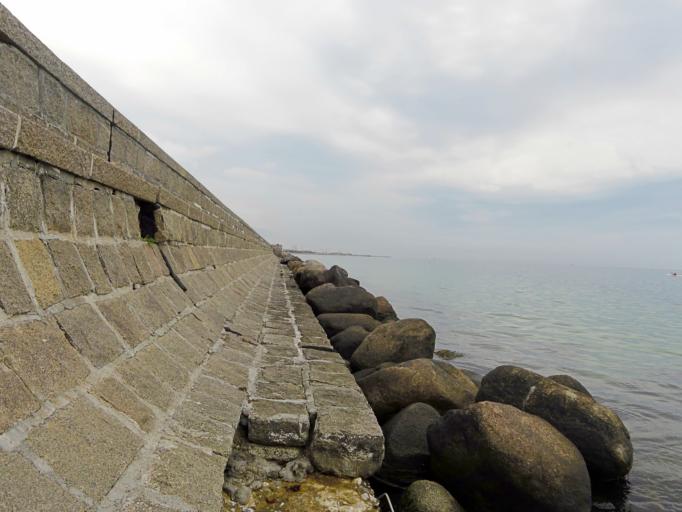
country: DK
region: Capital Region
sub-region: Gentofte Kommune
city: Charlottenlund
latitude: 55.7514
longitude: 12.5927
